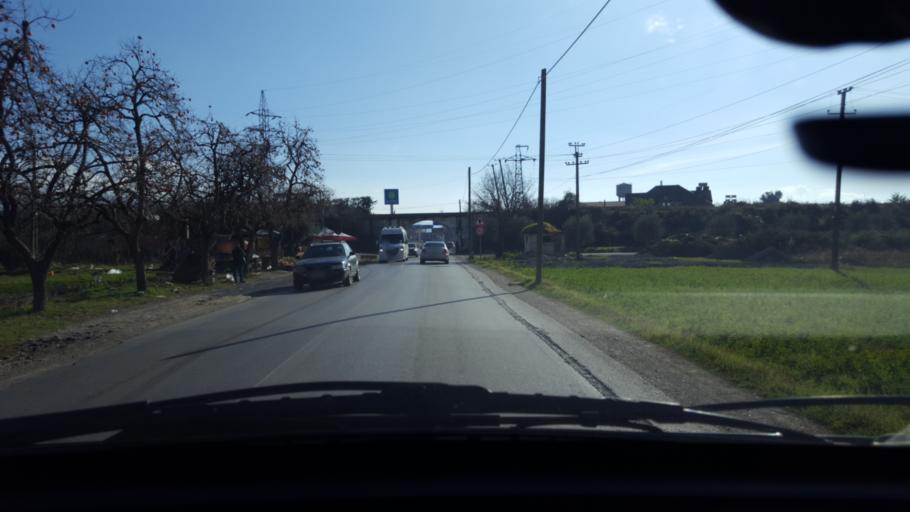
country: AL
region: Elbasan
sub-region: Rrethi i Elbasanit
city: Bradashesh
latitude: 41.1022
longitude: 20.0279
